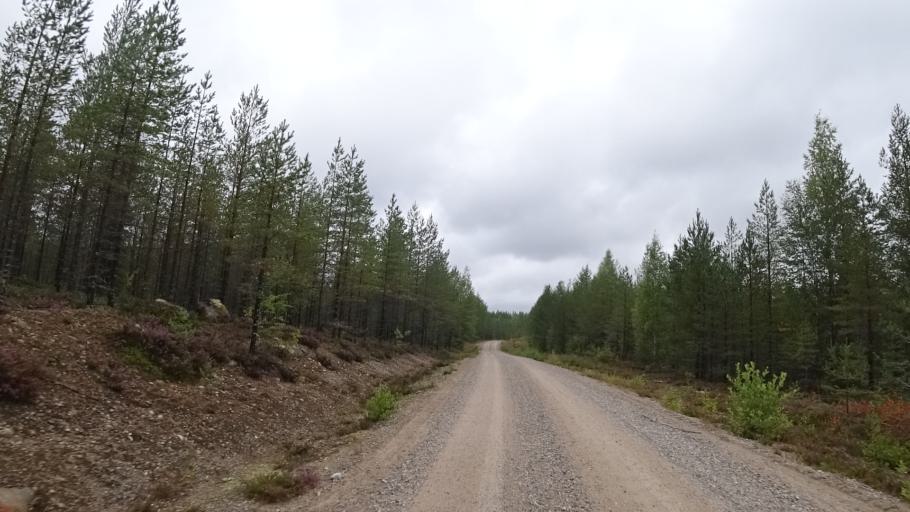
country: FI
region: North Karelia
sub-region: Pielisen Karjala
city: Lieksa
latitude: 63.5142
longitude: 30.1252
